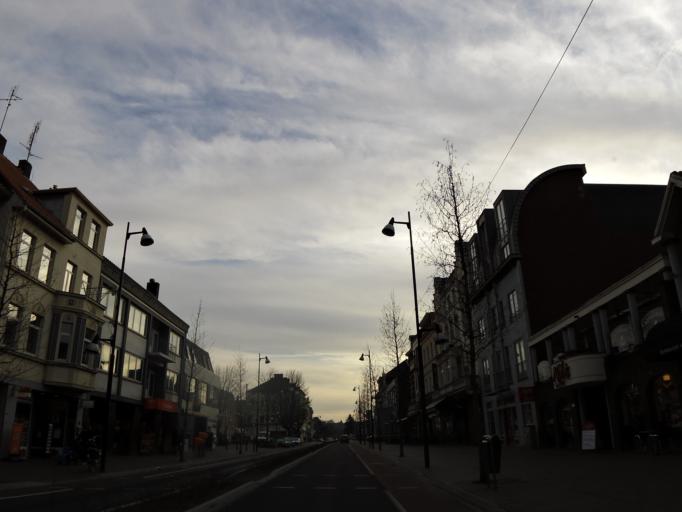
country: NL
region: Limburg
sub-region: Gemeente Vaals
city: Vaals
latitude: 50.7719
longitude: 6.0220
